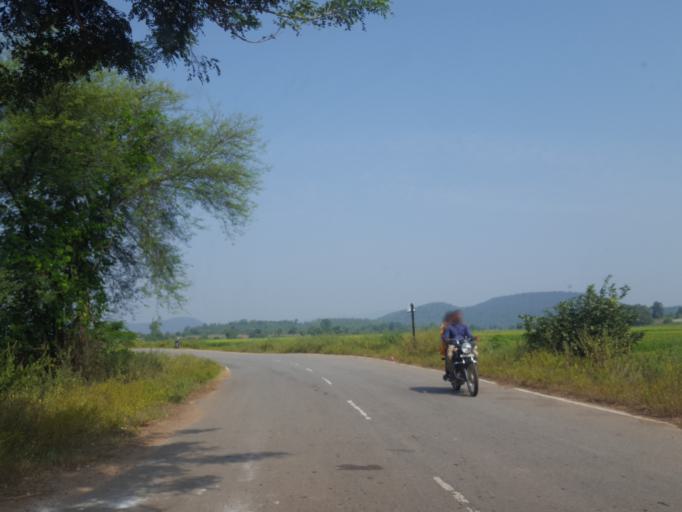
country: IN
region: Telangana
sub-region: Khammam
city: Yellandu
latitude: 17.6547
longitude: 80.2807
